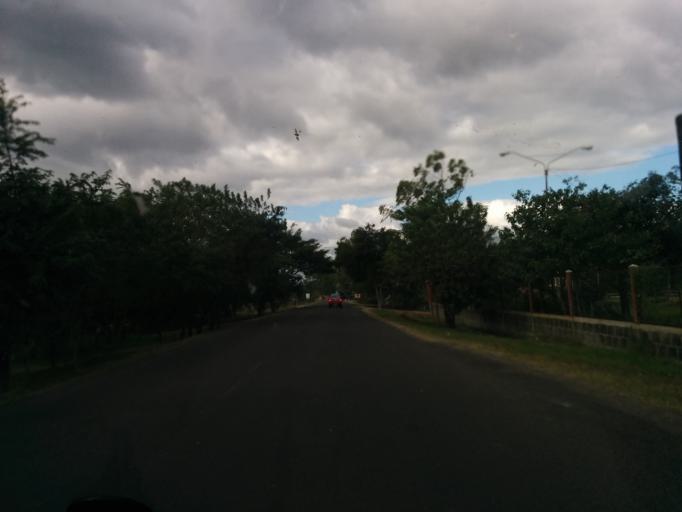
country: NI
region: Esteli
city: Esteli
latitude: 13.1456
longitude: -86.3682
